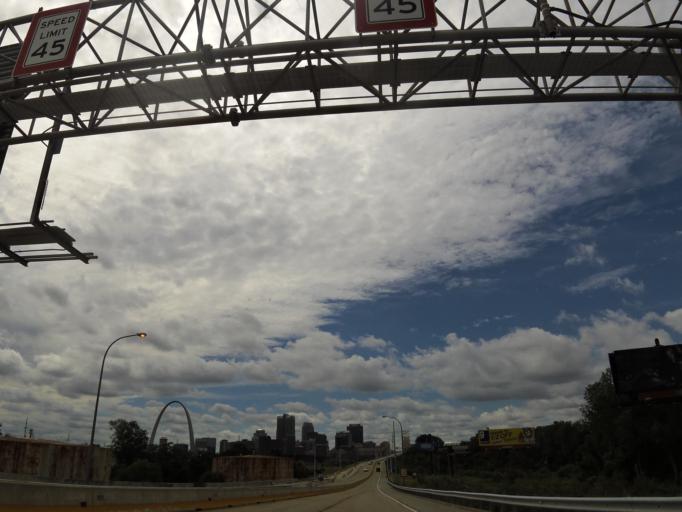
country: US
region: Illinois
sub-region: Saint Clair County
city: East Saint Louis
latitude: 38.6300
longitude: -90.1662
